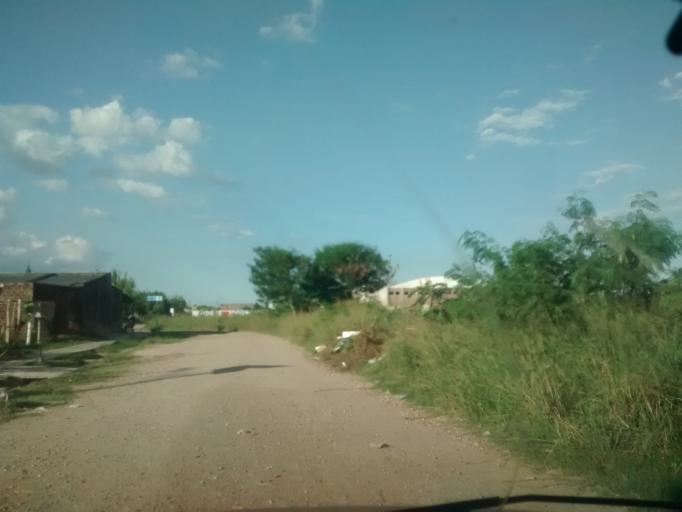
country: AR
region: Chaco
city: Fontana
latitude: -27.4578
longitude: -59.0284
